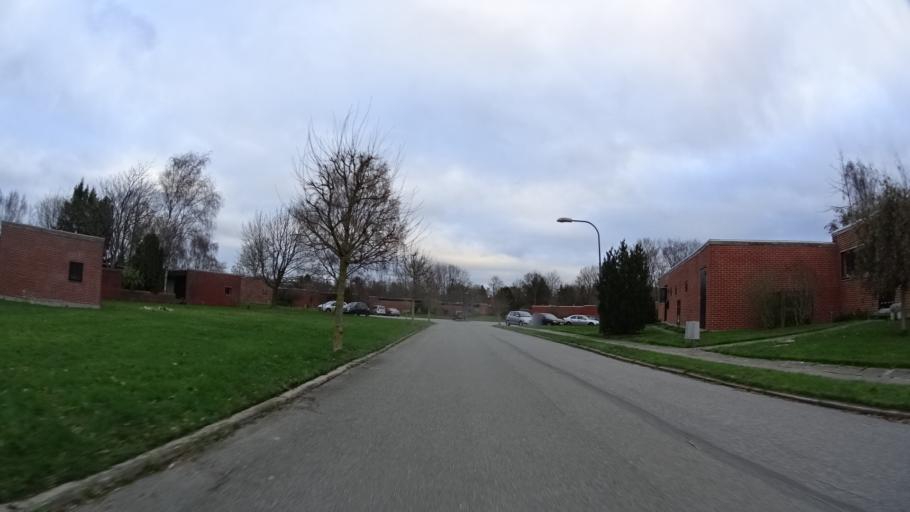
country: DK
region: Central Jutland
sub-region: Arhus Kommune
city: Stavtrup
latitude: 56.1608
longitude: 10.1173
